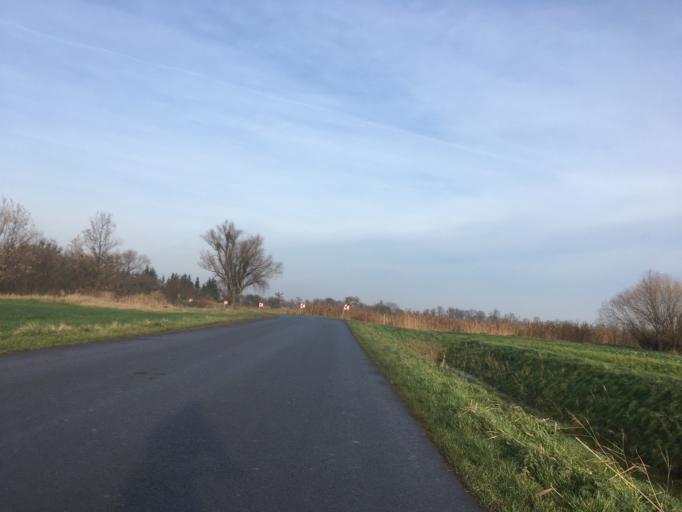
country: DE
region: Brandenburg
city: Bad Freienwalde
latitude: 52.7819
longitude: 14.0831
